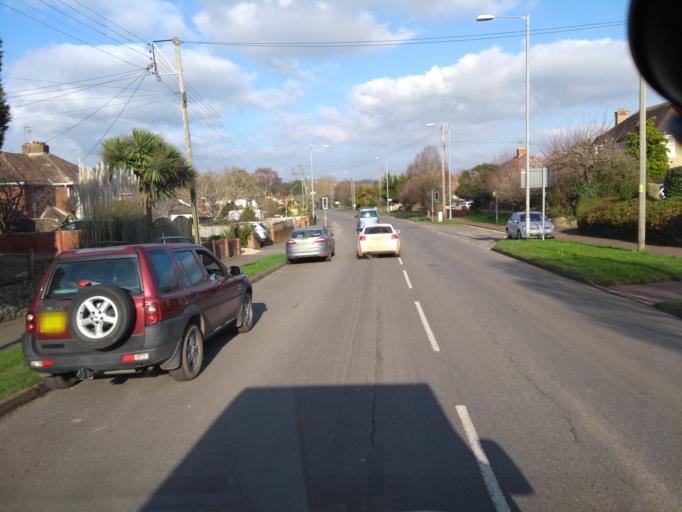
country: GB
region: England
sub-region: Somerset
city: Taunton
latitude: 51.0193
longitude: -3.0734
